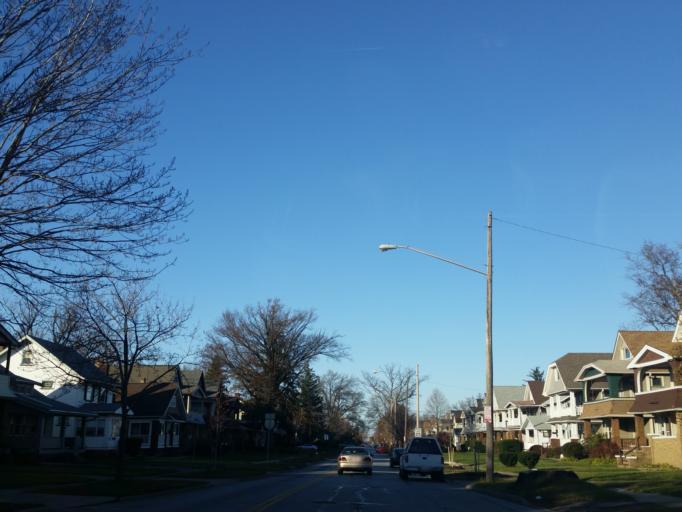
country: US
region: Ohio
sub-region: Cuyahoga County
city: Lakewood
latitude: 41.4715
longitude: -81.7897
